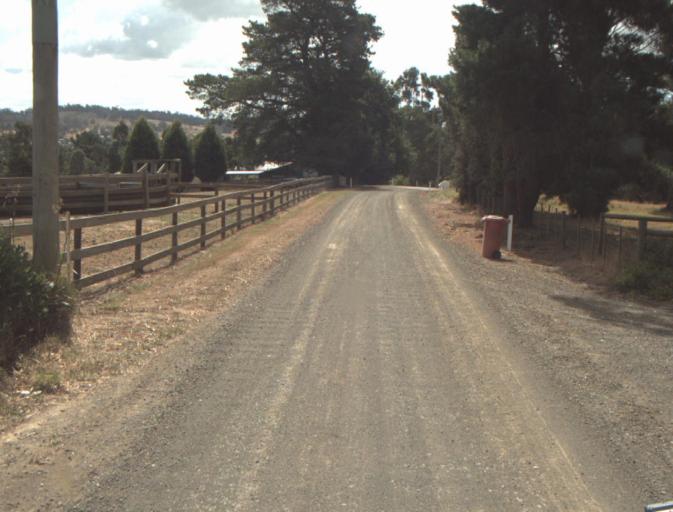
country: AU
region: Tasmania
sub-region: Launceston
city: Mayfield
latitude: -41.2981
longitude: 146.9888
